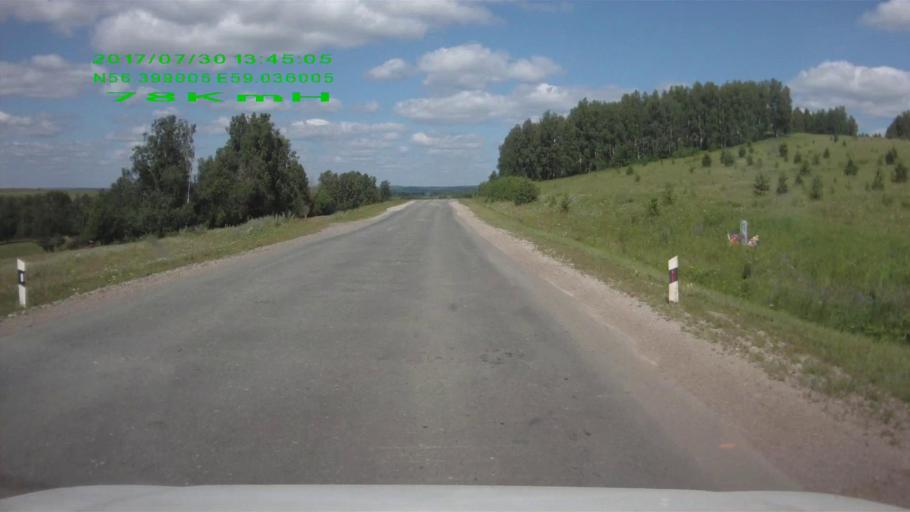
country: RU
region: Sverdlovsk
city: Mikhaylovsk
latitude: 56.3992
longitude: 59.0360
